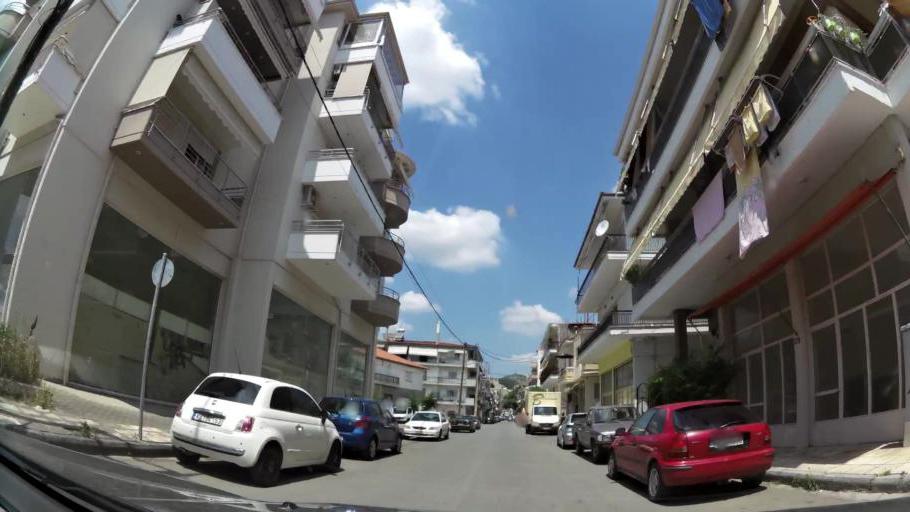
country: GR
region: West Macedonia
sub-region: Nomos Kozanis
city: Kozani
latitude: 40.2959
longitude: 21.7932
